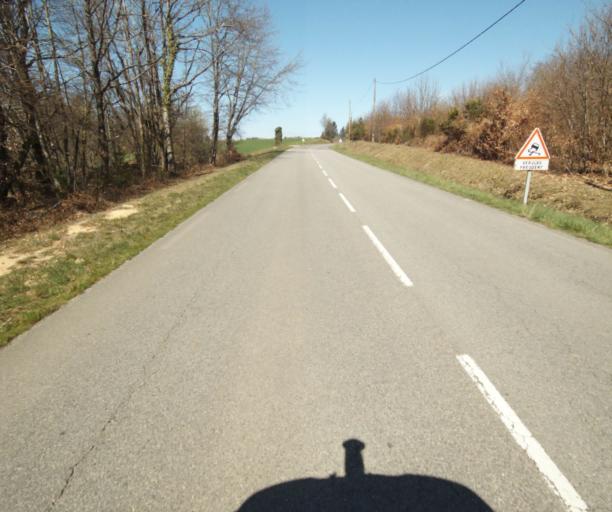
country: FR
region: Limousin
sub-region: Departement de la Correze
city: Saint-Mexant
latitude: 45.2990
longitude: 1.6721
